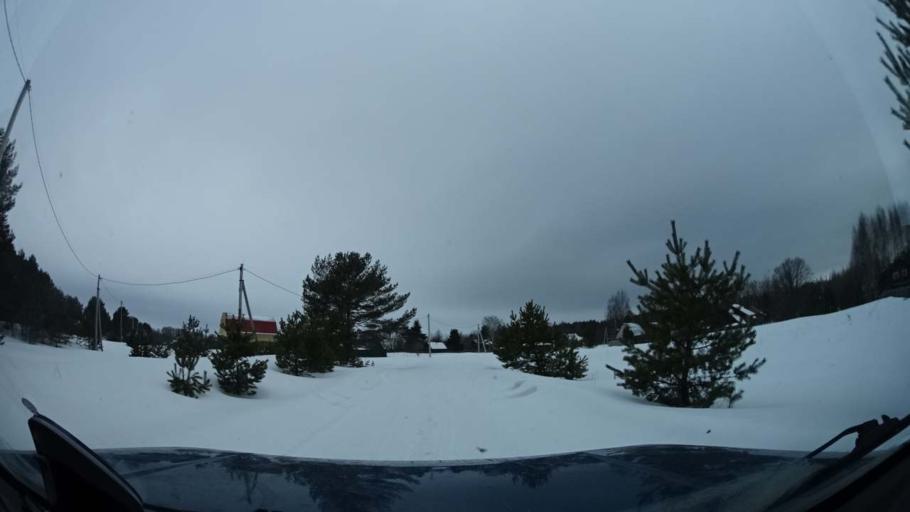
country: RU
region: Tverskaya
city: Radchenko
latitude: 56.7051
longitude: 36.4005
